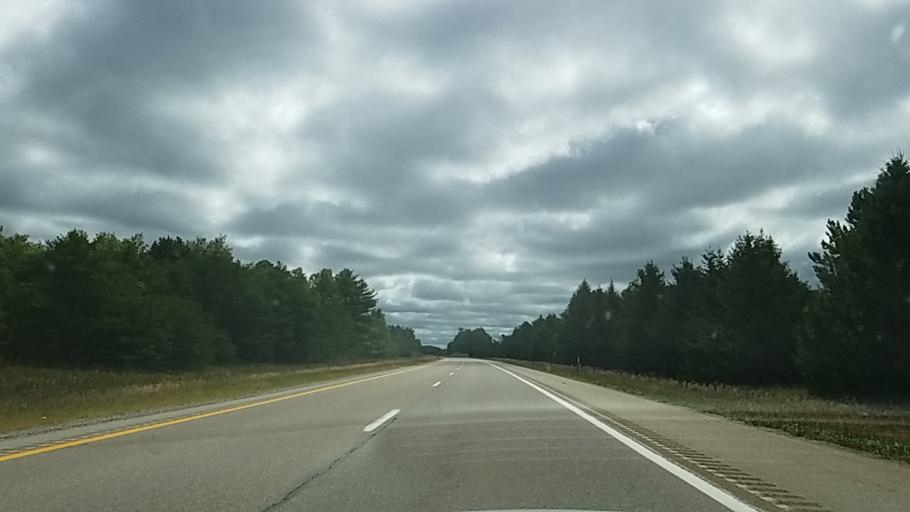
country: US
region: Michigan
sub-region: Roscommon County
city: Roscommon
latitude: 44.5426
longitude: -84.6962
